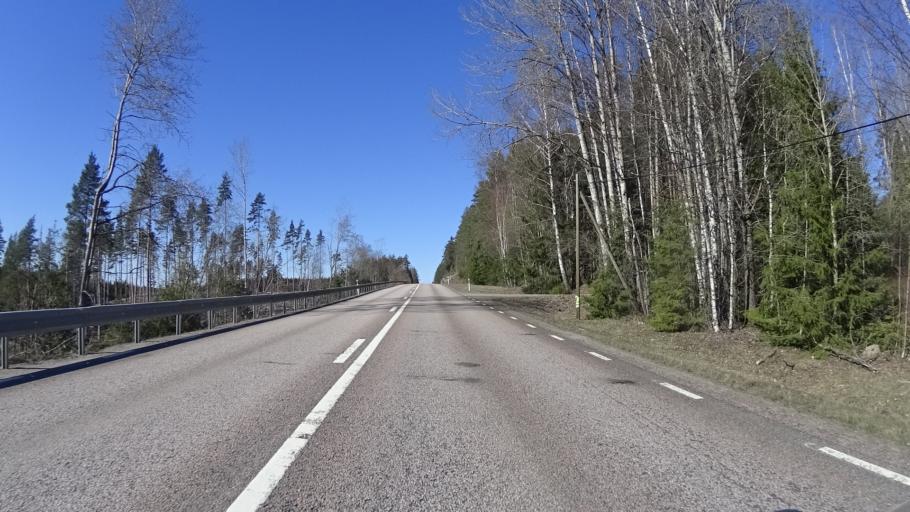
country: SE
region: Vaermland
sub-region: Karlstads Kommun
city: Edsvalla
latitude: 59.5832
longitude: 13.0152
